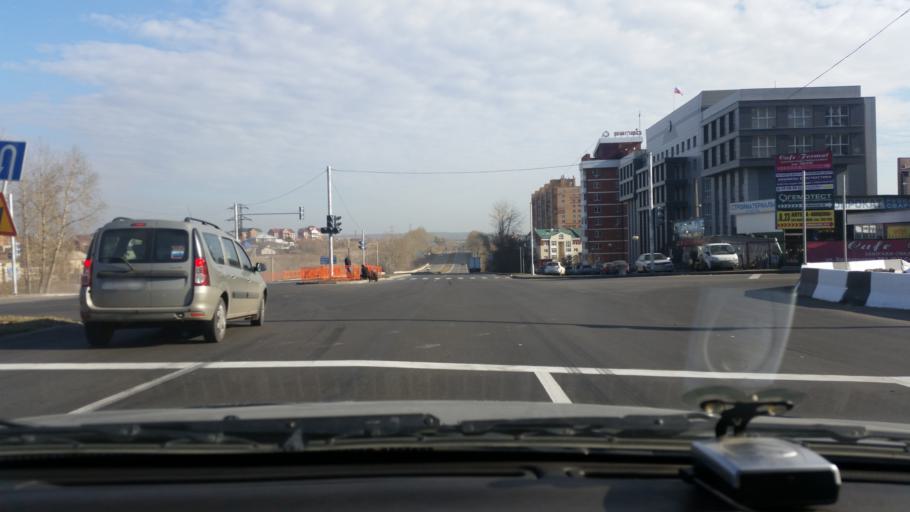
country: RU
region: Irkutsk
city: Dzerzhinsk
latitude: 52.2602
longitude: 104.3570
